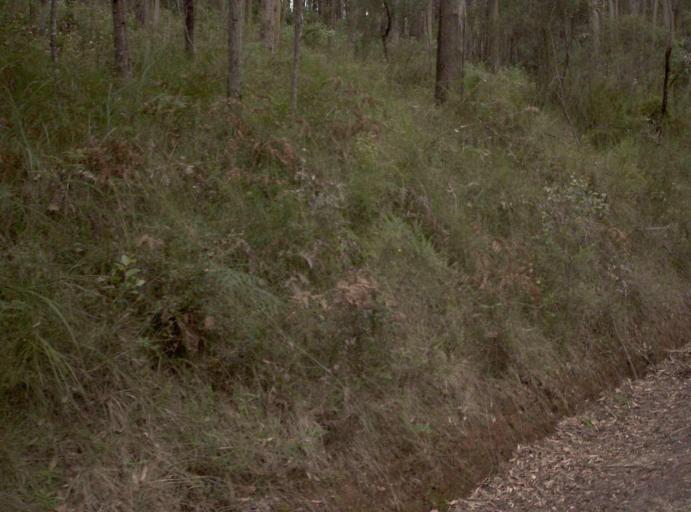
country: AU
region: New South Wales
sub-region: Bombala
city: Bombala
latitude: -37.4060
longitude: 149.2014
